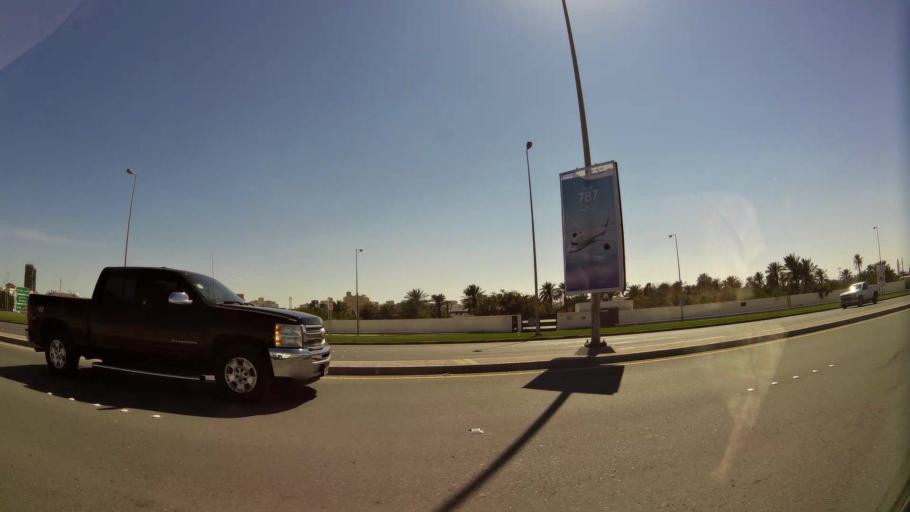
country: BH
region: Muharraq
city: Al Hadd
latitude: 26.2556
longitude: 50.6533
